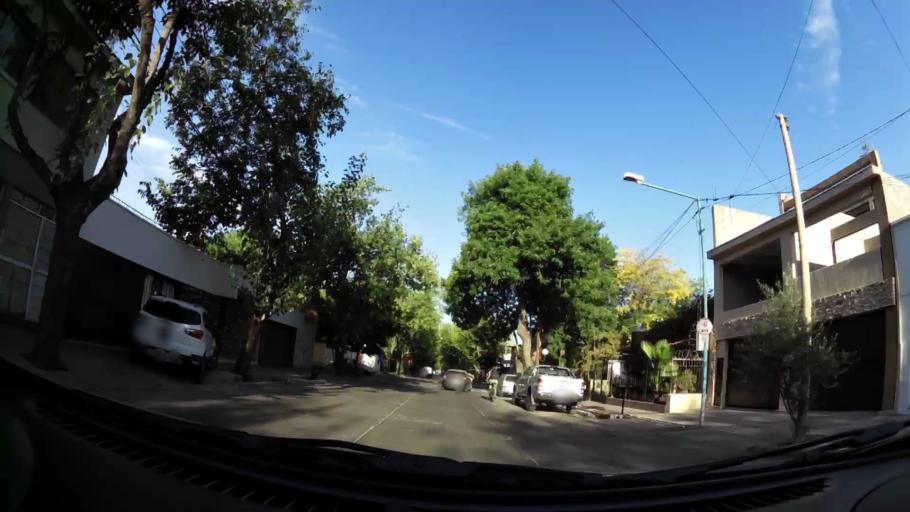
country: AR
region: Mendoza
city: Mendoza
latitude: -32.9033
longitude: -68.8503
